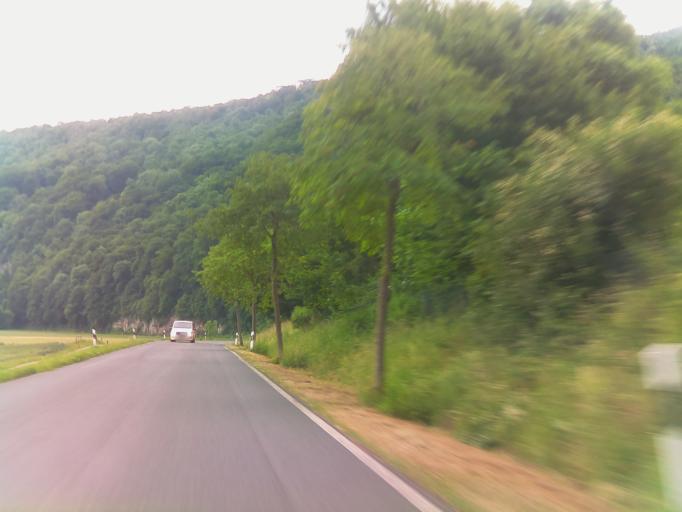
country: DE
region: Lower Saxony
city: Pegestorf
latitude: 51.9251
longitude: 9.4756
